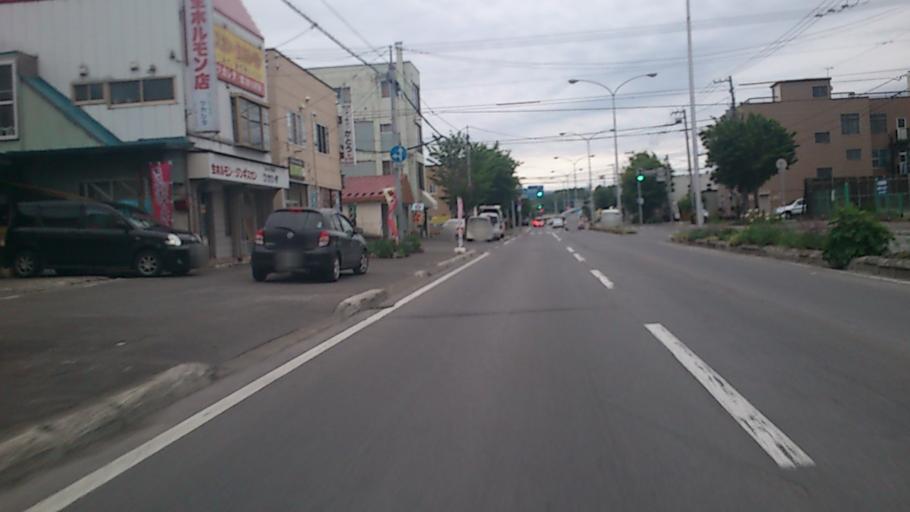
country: JP
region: Hokkaido
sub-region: Asahikawa-shi
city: Asahikawa
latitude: 43.7642
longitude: 142.3725
